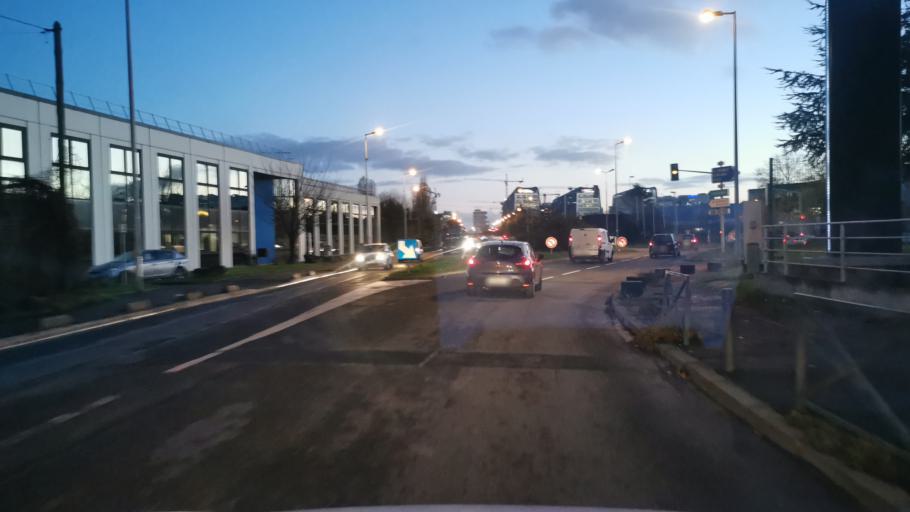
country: FR
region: Ile-de-France
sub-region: Departement du Val-de-Marne
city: Fontenay-sous-Bois
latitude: 48.8604
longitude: 2.4901
